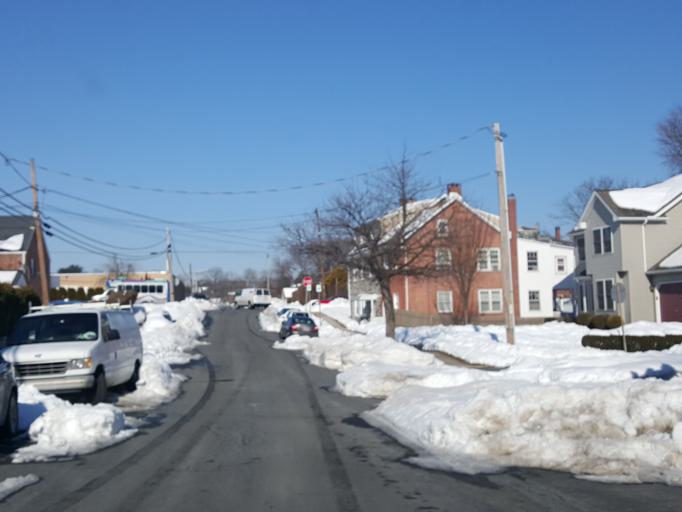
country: US
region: Pennsylvania
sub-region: Berks County
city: Kenhorst
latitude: 40.3129
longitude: -75.9418
